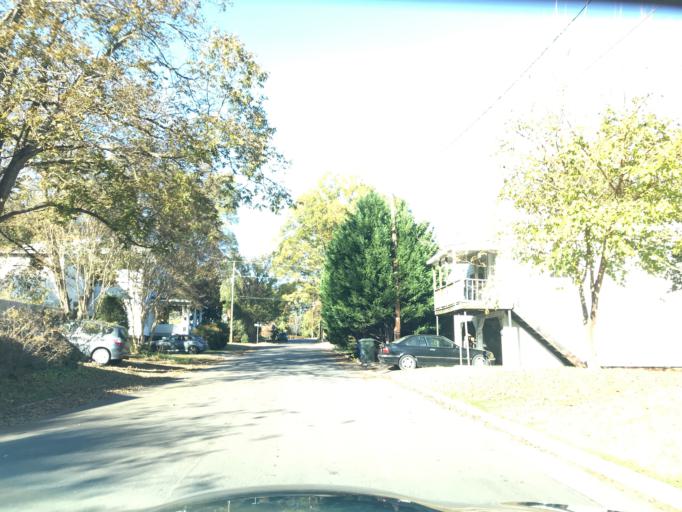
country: US
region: North Carolina
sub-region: Wake County
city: Raleigh
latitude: 35.7963
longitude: -78.6281
